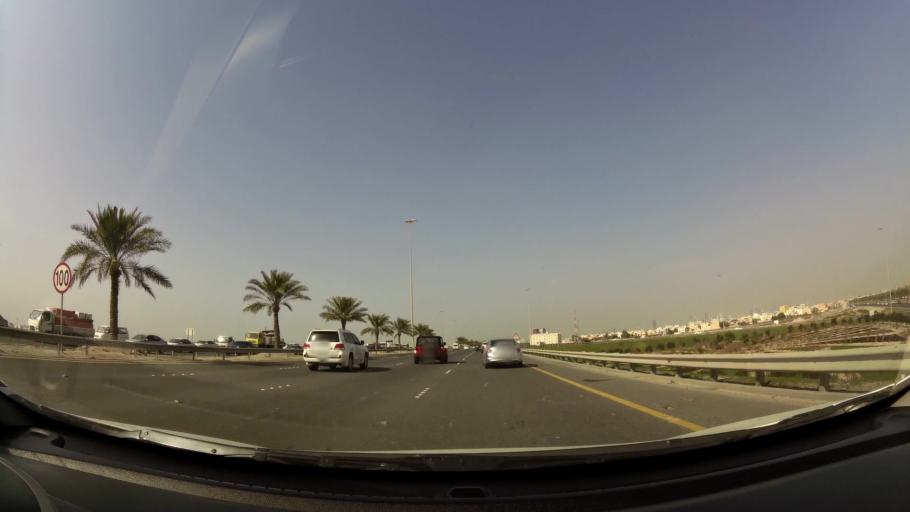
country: BH
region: Northern
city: Madinat `Isa
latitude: 26.1865
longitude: 50.5037
